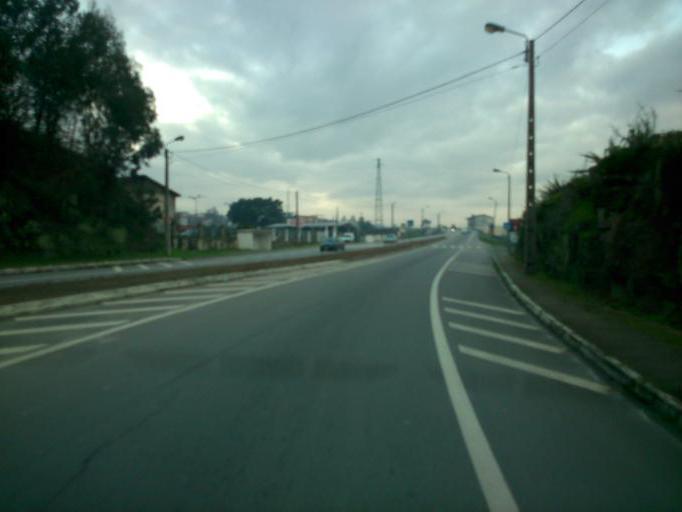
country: PT
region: Braga
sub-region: Barcelos
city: Barcelos
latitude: 41.5197
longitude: -8.5871
